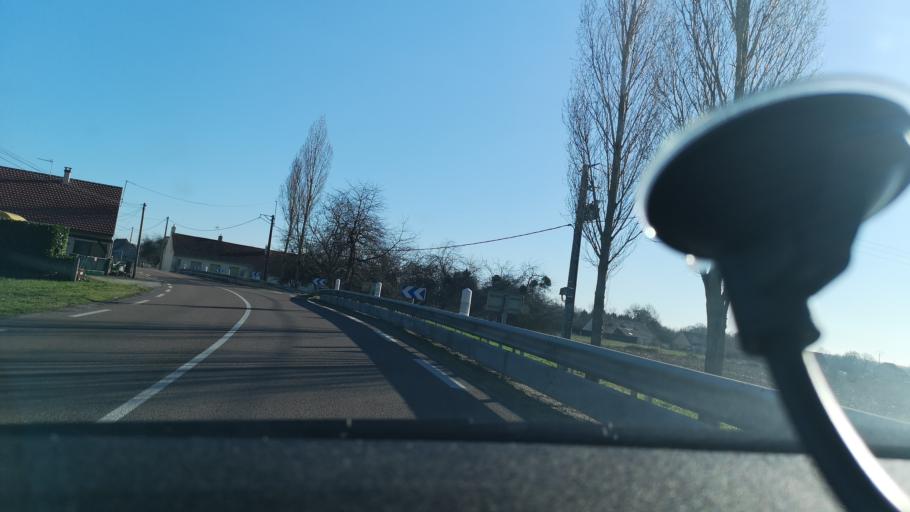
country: FR
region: Bourgogne
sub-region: Departement de Saone-et-Loire
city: Ouroux-sur-Saone
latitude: 46.7598
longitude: 4.9934
